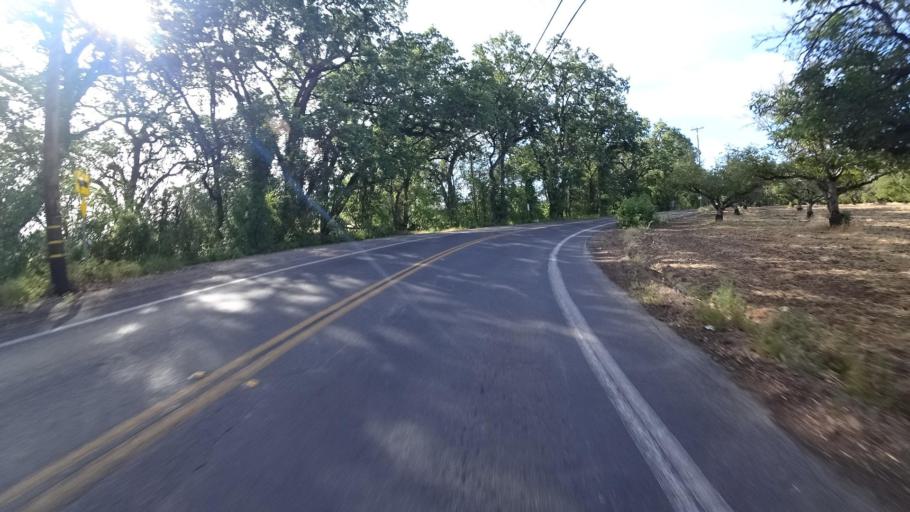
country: US
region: California
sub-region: Lake County
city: Lakeport
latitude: 39.0105
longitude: -122.8947
